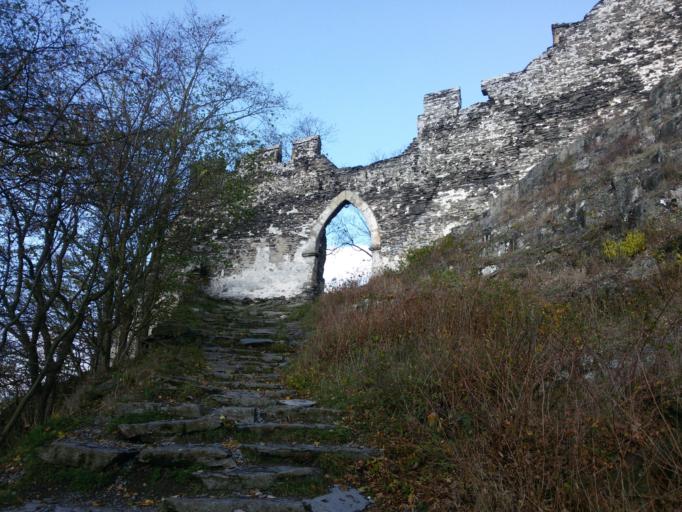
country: CZ
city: Doksy
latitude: 50.5383
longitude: 14.7188
